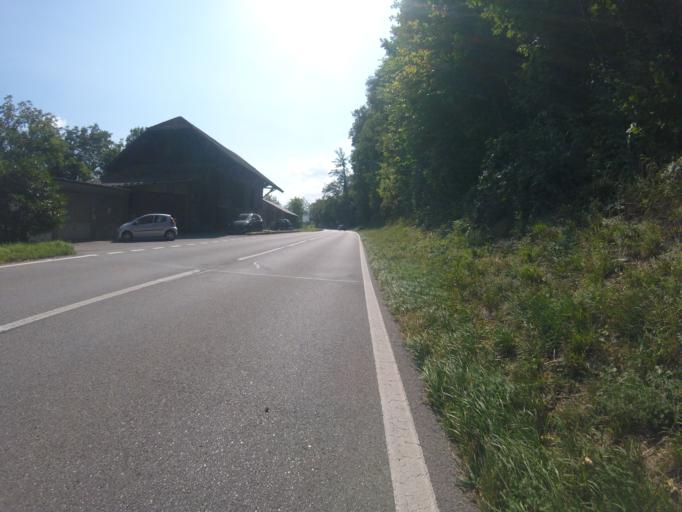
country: CH
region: Bern
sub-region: Bern-Mittelland District
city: Toffen
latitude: 46.8754
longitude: 7.4927
